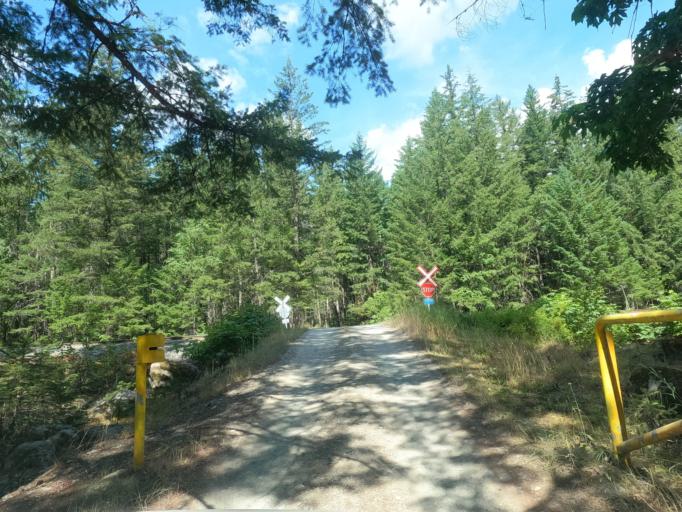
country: CA
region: British Columbia
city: Pemberton
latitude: 50.3513
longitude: -122.7296
